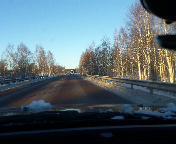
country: SE
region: Gaevleborg
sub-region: Ljusdals Kommun
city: Jaervsoe
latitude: 61.7582
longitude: 16.1606
